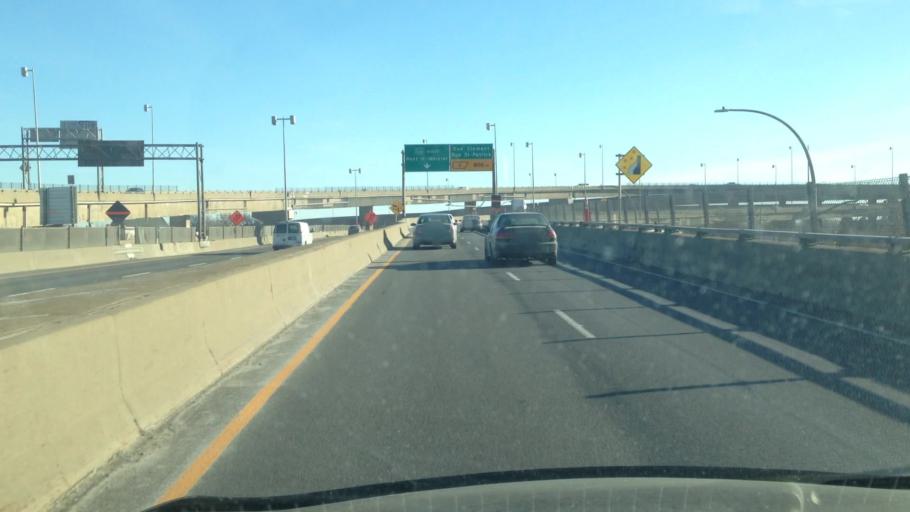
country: CA
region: Quebec
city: Montreal-Ouest
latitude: 45.4421
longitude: -73.6546
